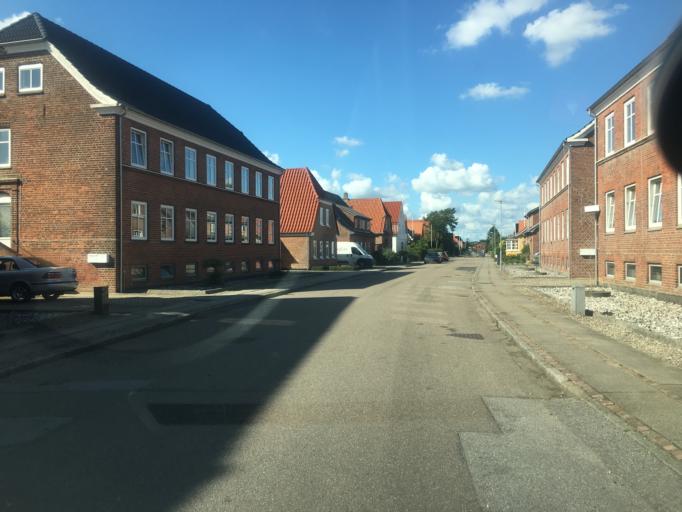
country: DK
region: South Denmark
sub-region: Tonder Kommune
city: Tonder
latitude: 54.9315
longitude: 8.8559
